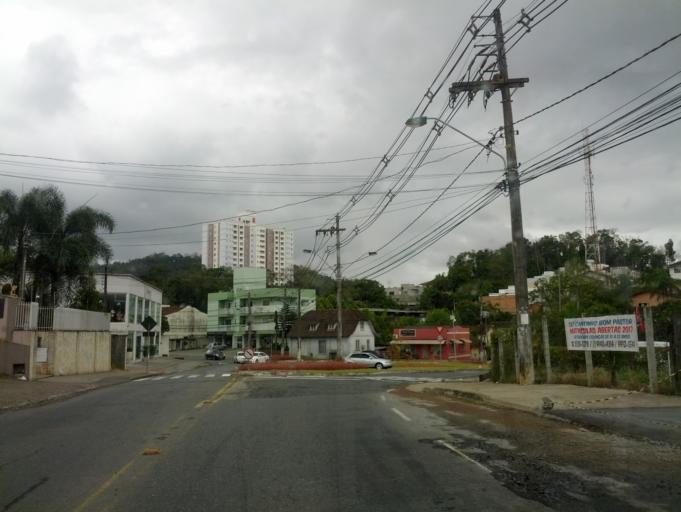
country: BR
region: Santa Catarina
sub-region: Blumenau
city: Blumenau
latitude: -26.9156
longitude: -49.1100
